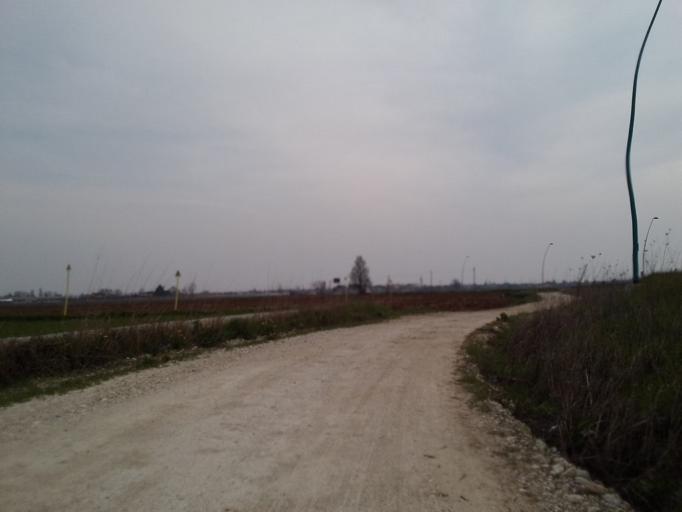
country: IT
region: Veneto
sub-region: Provincia di Verona
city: Povegliano Veronese
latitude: 45.3629
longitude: 10.8845
